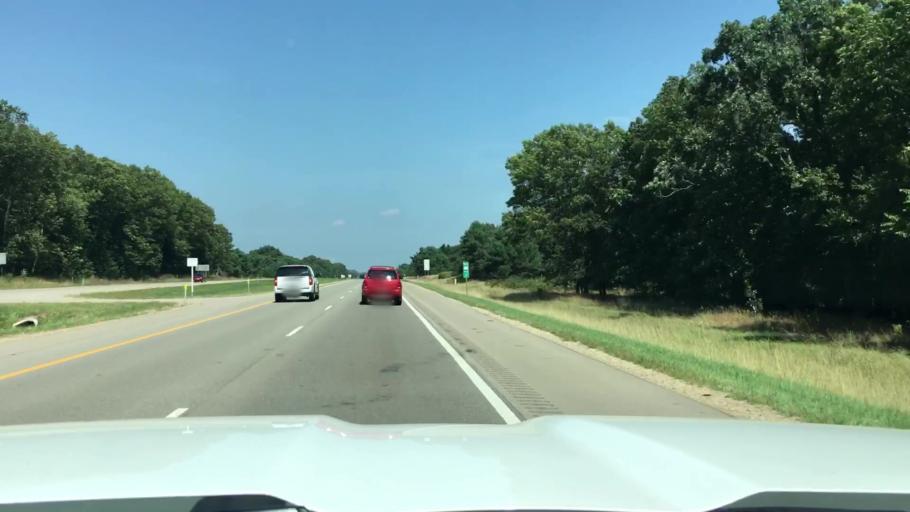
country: US
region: Michigan
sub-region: Kalamazoo County
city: Portage
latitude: 42.2074
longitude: -85.6437
